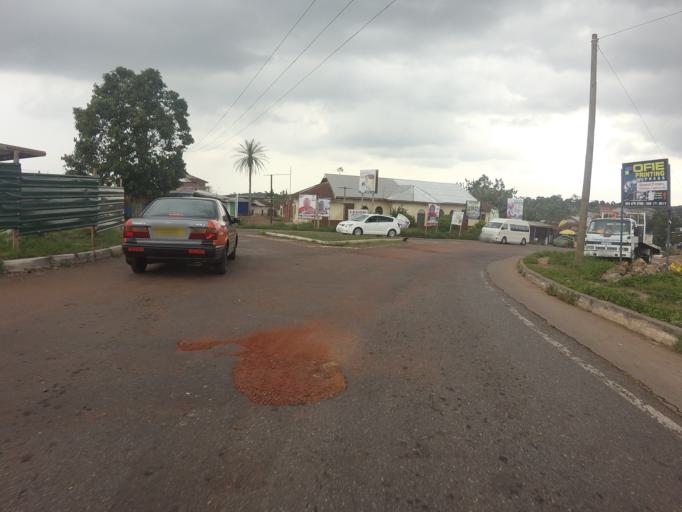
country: GH
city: Akropong
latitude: 5.9389
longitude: -0.1162
